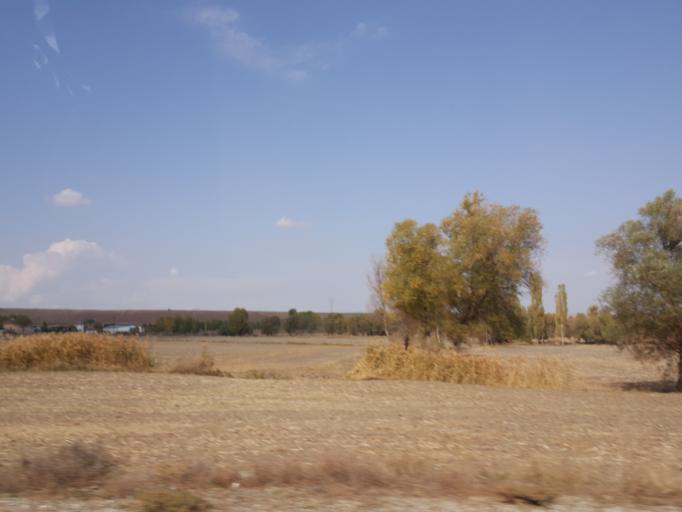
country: TR
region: Corum
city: Alaca
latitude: 40.1419
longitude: 34.8253
